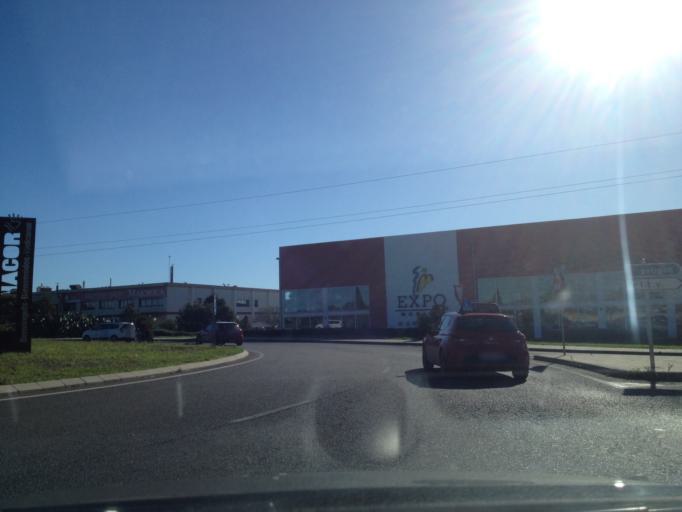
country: ES
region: Balearic Islands
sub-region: Illes Balears
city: Manacor
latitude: 39.5730
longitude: 3.1863
